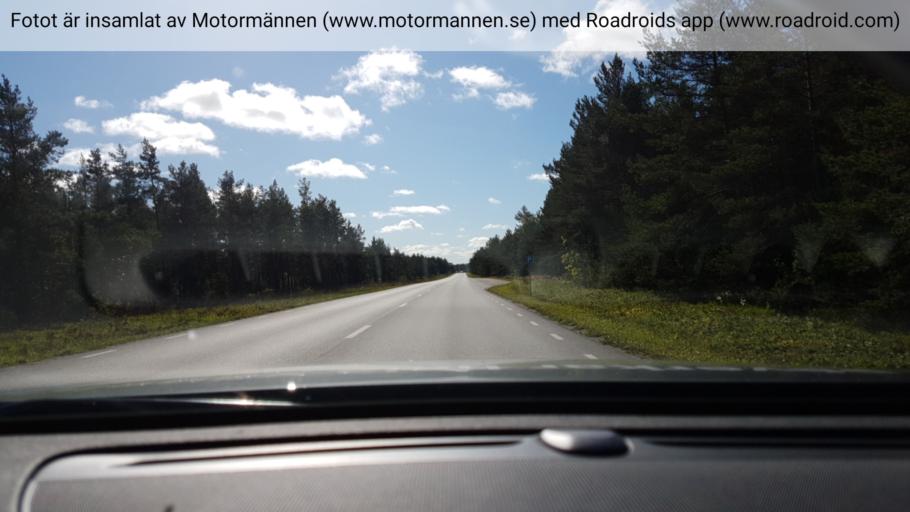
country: SE
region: Gotland
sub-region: Gotland
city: Slite
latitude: 57.7319
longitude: 18.7905
